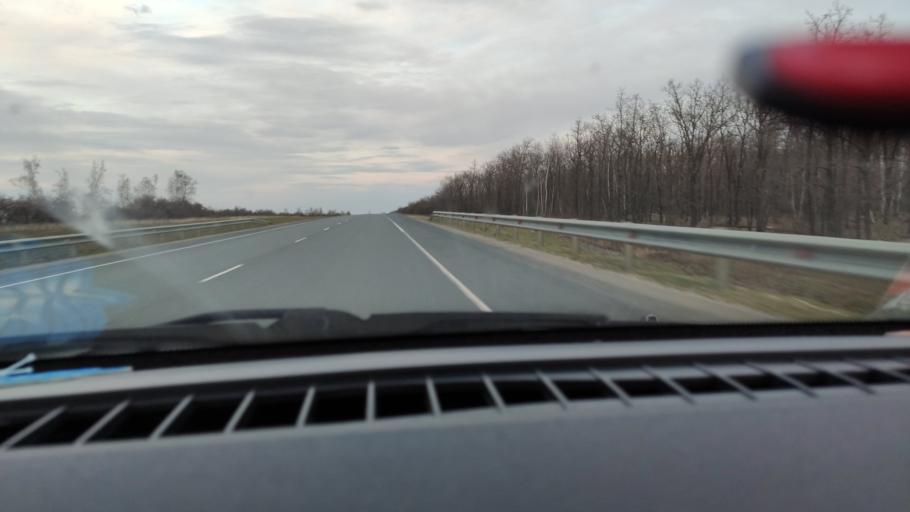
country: RU
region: Saratov
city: Yelshanka
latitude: 51.8206
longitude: 46.3449
